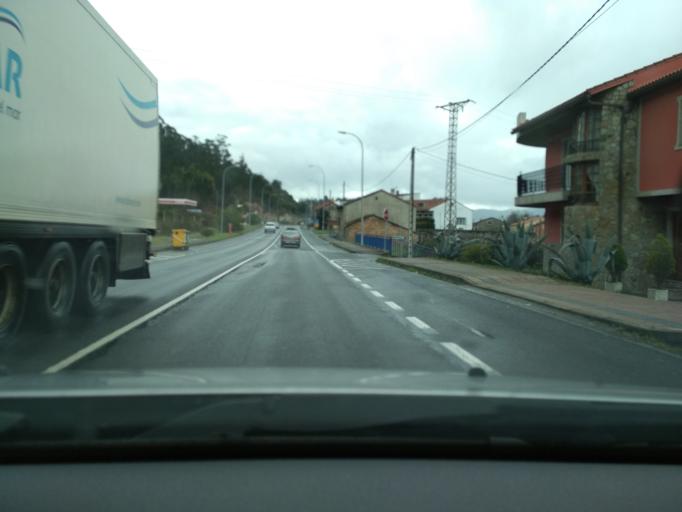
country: ES
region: Galicia
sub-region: Provincia da Coruna
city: Padron
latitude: 42.7625
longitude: -8.6517
